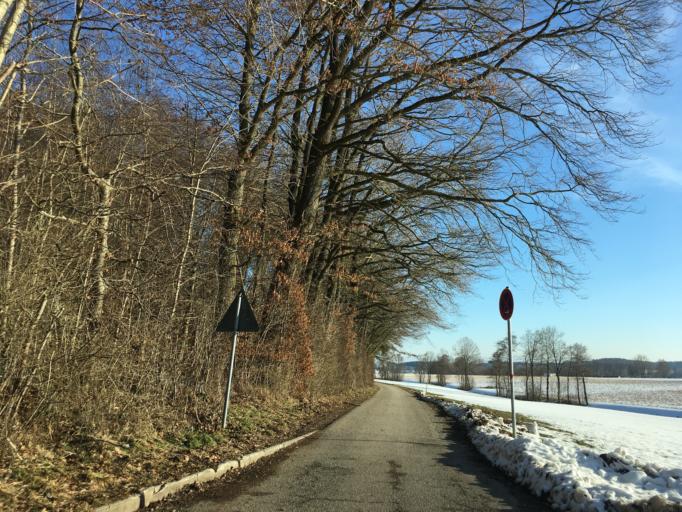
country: DE
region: Bavaria
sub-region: Upper Bavaria
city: Steinhoring
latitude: 48.0985
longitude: 12.0374
